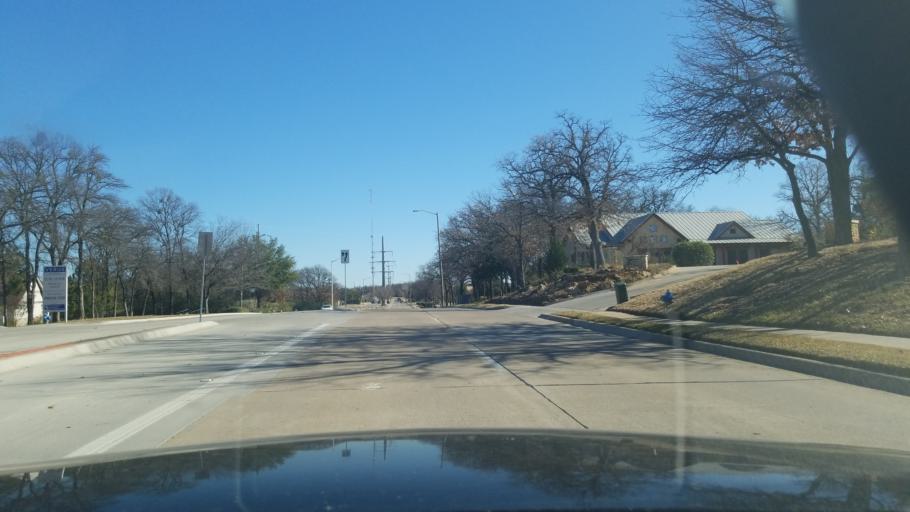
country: US
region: Texas
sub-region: Denton County
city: Corinth
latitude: 33.1818
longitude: -97.0965
